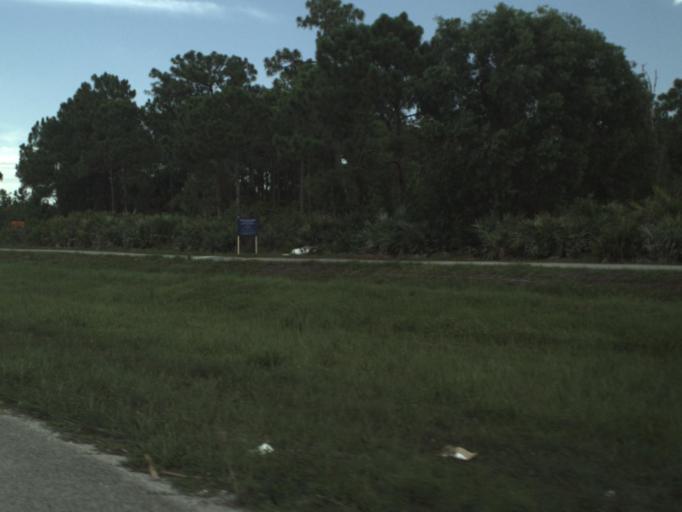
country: US
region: Florida
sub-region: Martin County
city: Port Salerno
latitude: 27.1576
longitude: -80.2217
